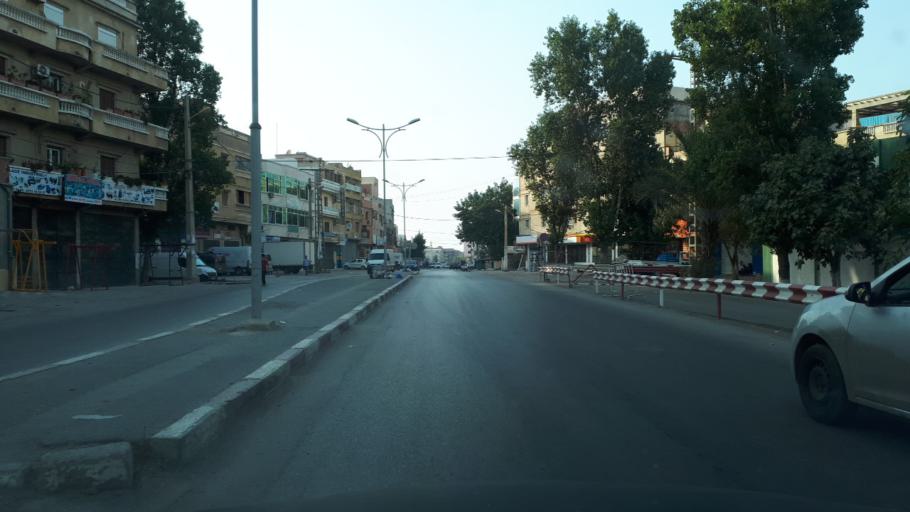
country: DZ
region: Alger
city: Dar el Beida
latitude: 36.7310
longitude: 3.2361
